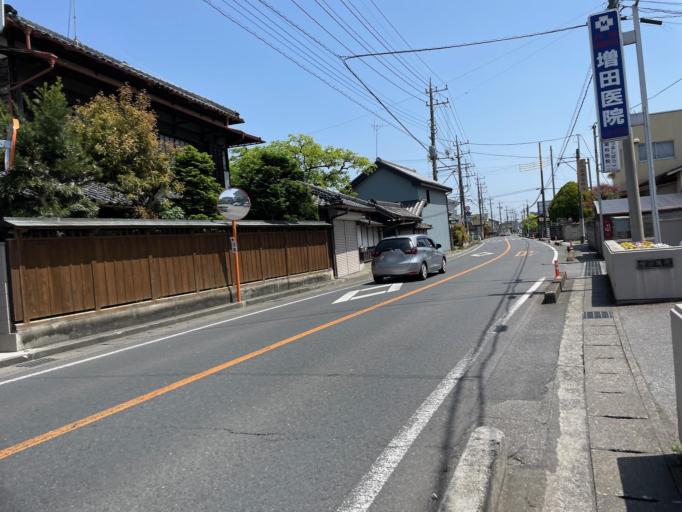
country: JP
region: Tochigi
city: Ashikaga
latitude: 36.3035
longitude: 139.4608
